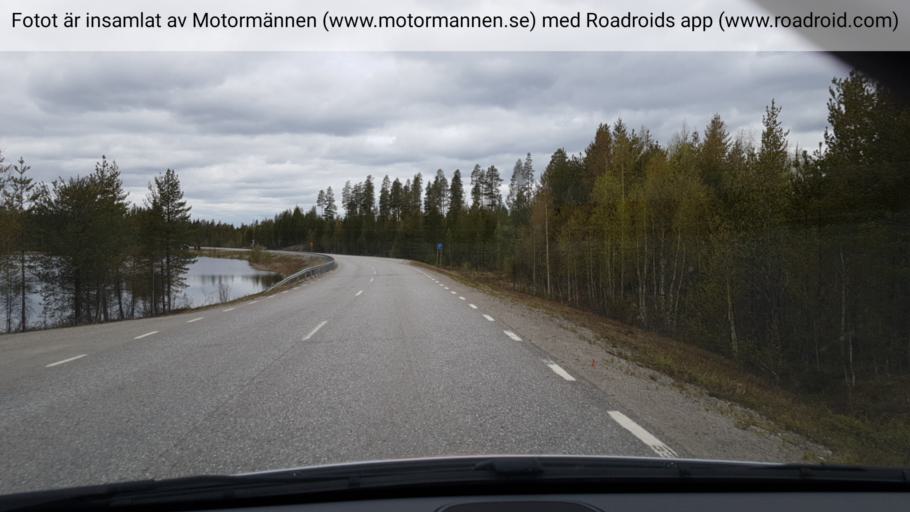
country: SE
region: Vaesterbotten
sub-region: Sorsele Kommun
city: Sorsele
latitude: 65.3127
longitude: 17.6635
